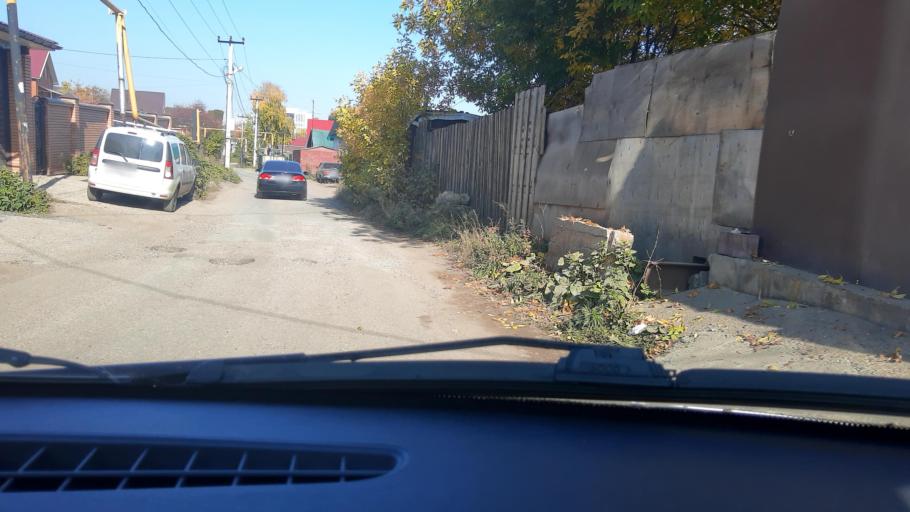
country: RU
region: Bashkortostan
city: Ufa
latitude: 54.7570
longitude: 56.0428
